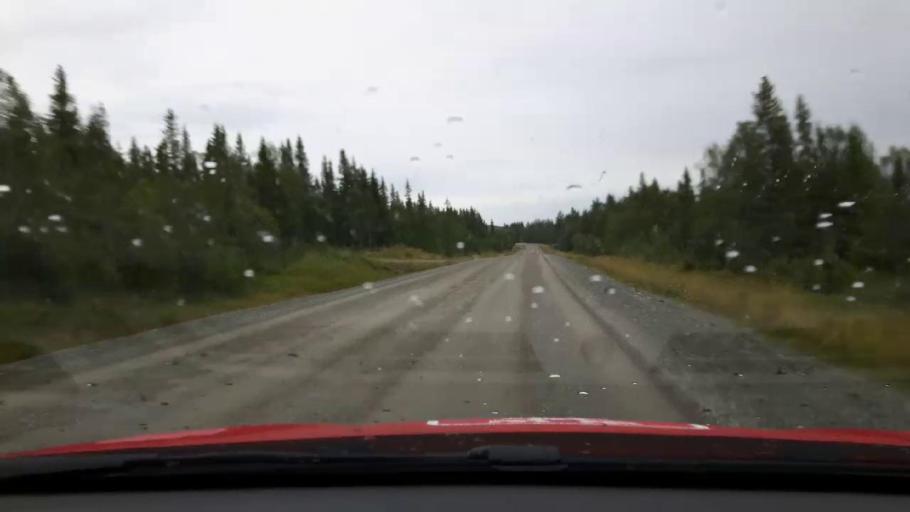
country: SE
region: Jaemtland
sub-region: Are Kommun
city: Are
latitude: 63.4667
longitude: 12.6151
